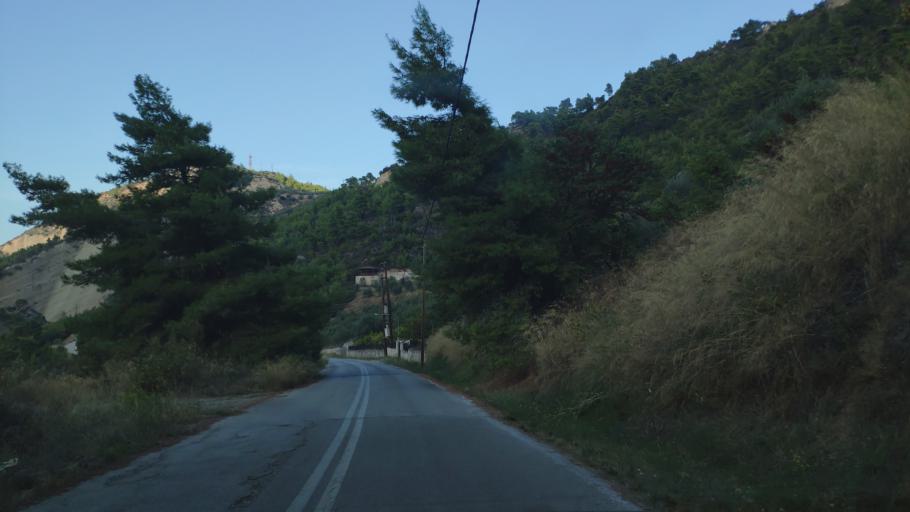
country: GR
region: West Greece
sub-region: Nomos Achaias
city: Aiyira
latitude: 38.0959
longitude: 22.4025
